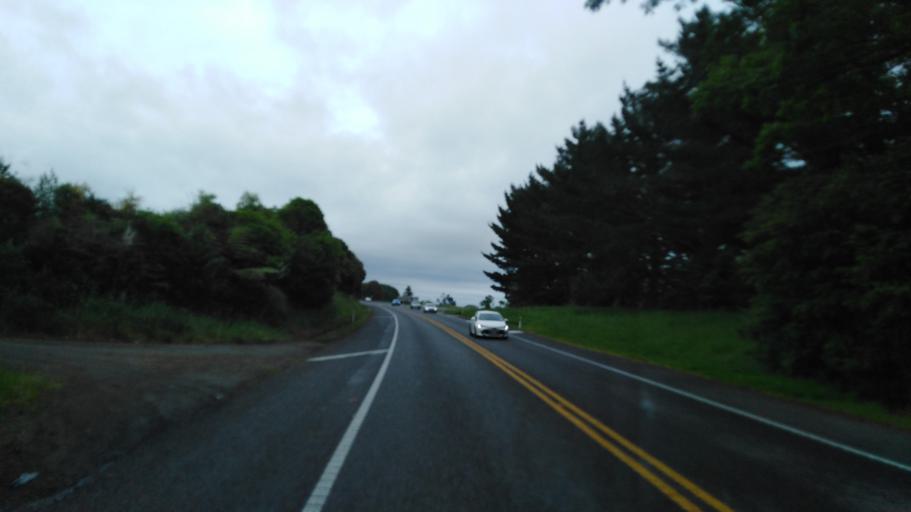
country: NZ
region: Wellington
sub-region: Kapiti Coast District
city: Otaki
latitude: -40.7340
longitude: 175.1952
